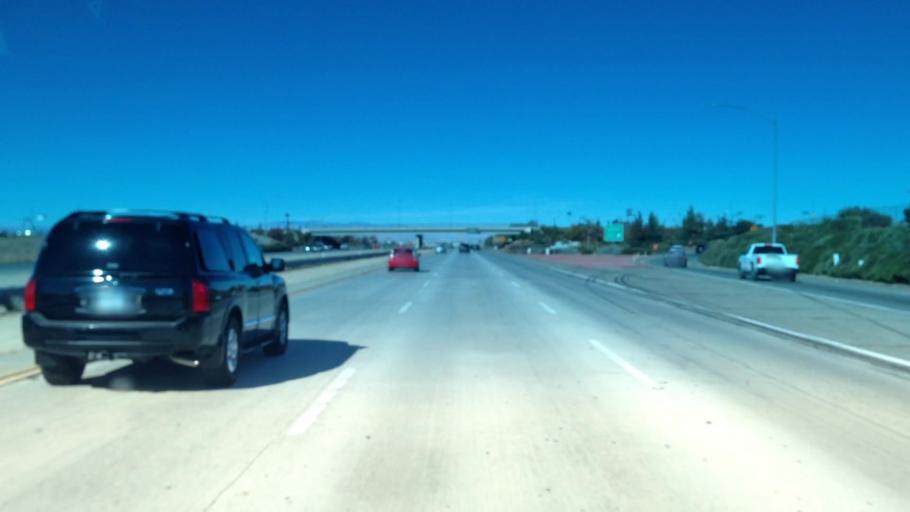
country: US
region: California
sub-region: Los Angeles County
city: Lancaster
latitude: 34.6573
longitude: -118.1530
